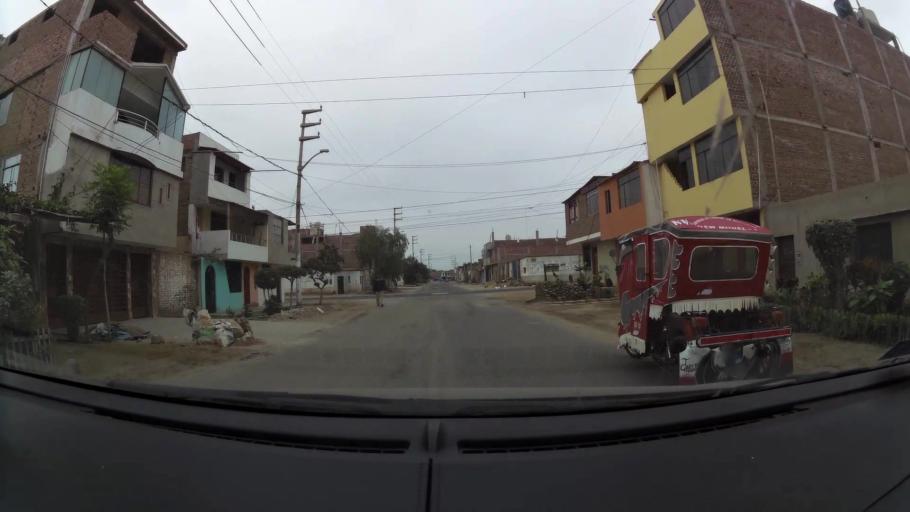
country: PE
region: La Libertad
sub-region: Provincia de Trujillo
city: La Esperanza
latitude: -8.0804
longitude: -79.0501
